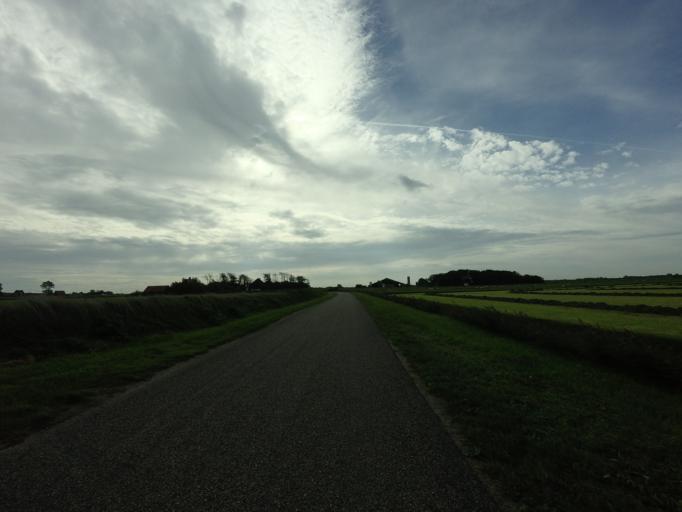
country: NL
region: North Holland
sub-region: Gemeente Texel
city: Den Burg
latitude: 53.0374
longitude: 4.7927
